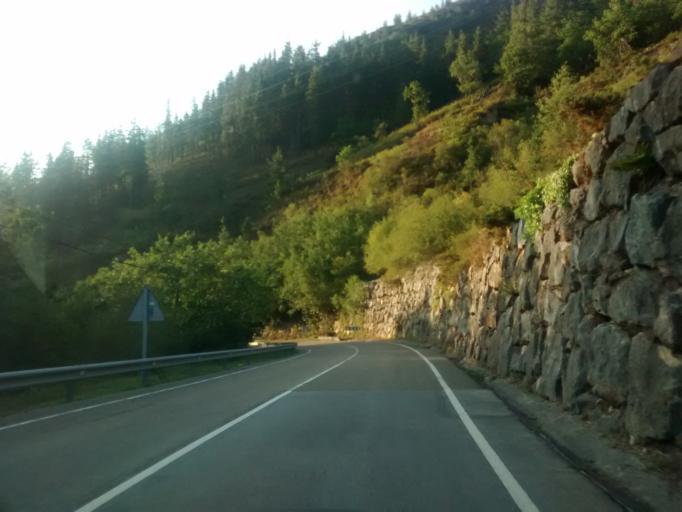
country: ES
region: Cantabria
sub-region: Provincia de Cantabria
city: Ruente
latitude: 43.1566
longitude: -4.2360
